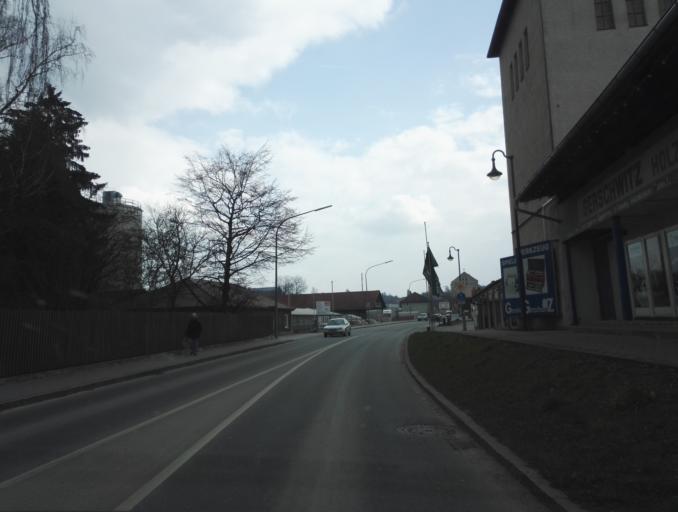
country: DE
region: Bavaria
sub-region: Lower Bavaria
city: Rottenburg an der Laaber
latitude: 48.7093
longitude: 12.0197
